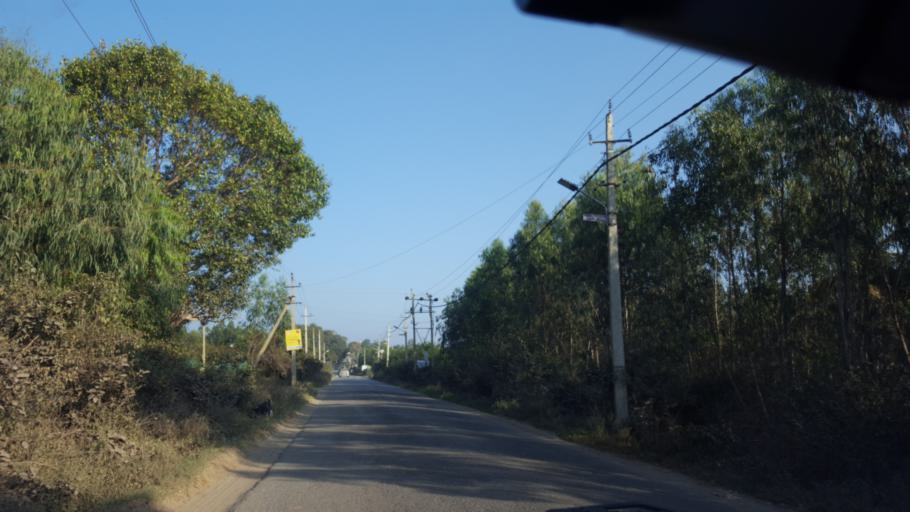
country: IN
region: Karnataka
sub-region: Bangalore Rural
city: Hoskote
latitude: 12.9174
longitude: 77.7608
